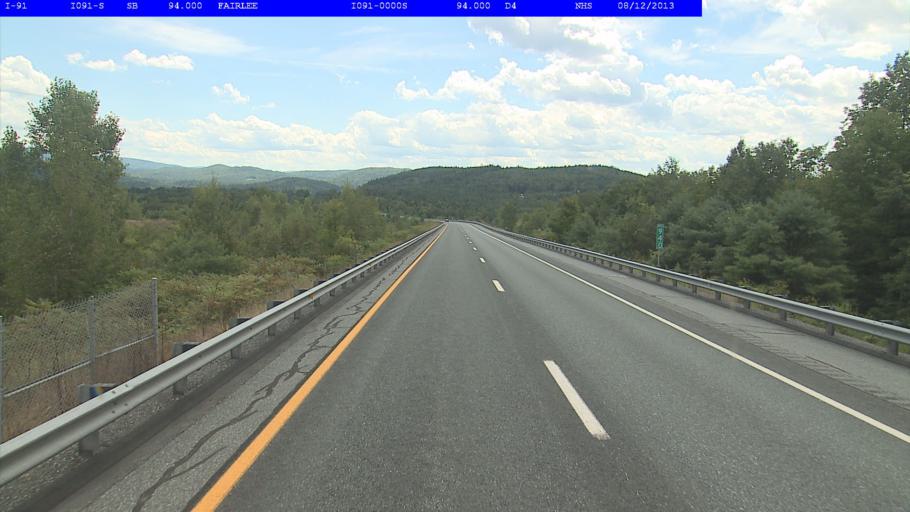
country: US
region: New Hampshire
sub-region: Grafton County
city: Orford
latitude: 43.9332
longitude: -72.1345
